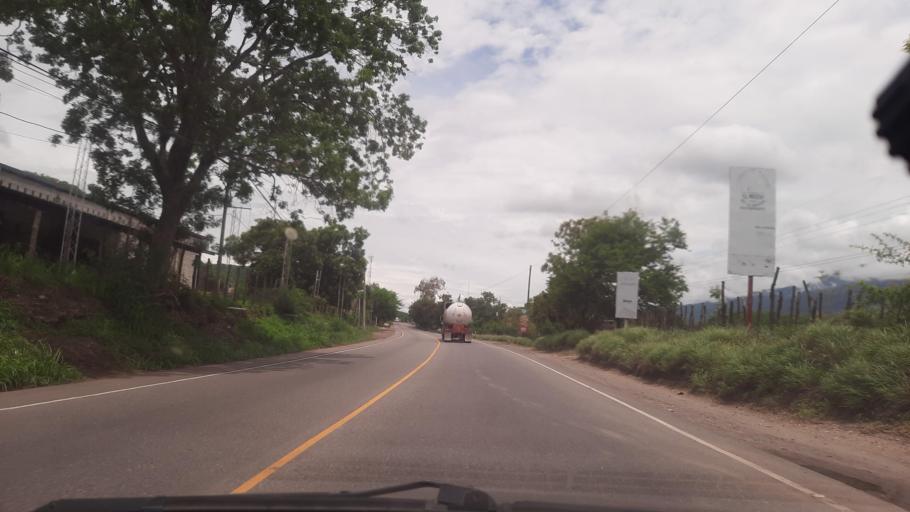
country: GT
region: Zacapa
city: Rio Hondo
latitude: 15.0846
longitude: -89.4782
